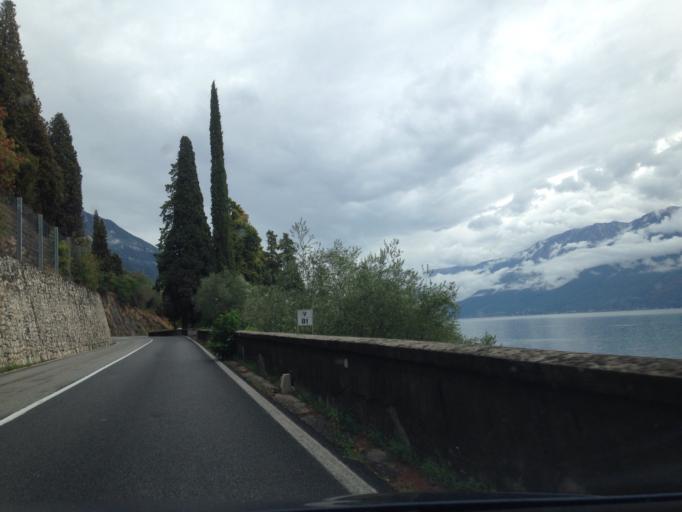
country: IT
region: Lombardy
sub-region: Provincia di Brescia
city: Gargnano
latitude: 45.6659
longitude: 10.6472
